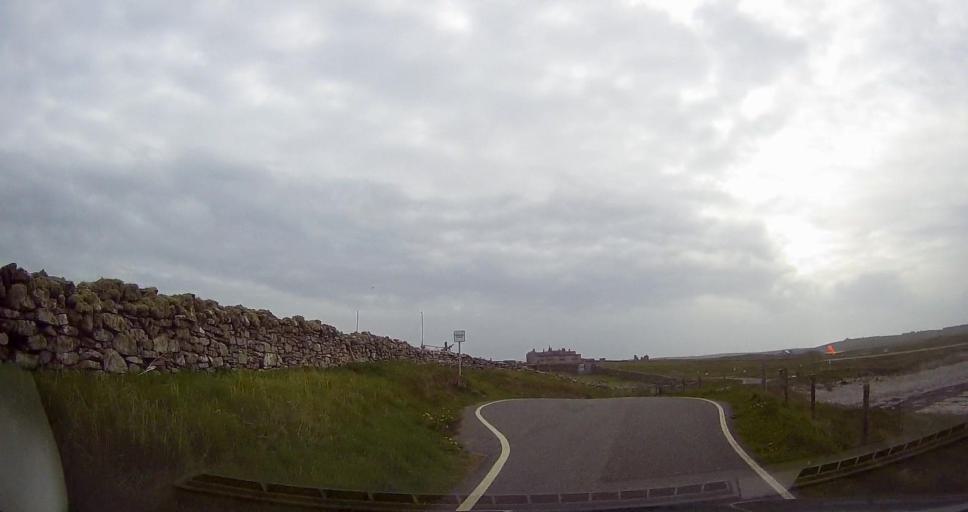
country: GB
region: Scotland
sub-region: Shetland Islands
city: Sandwick
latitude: 59.8723
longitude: -1.2799
